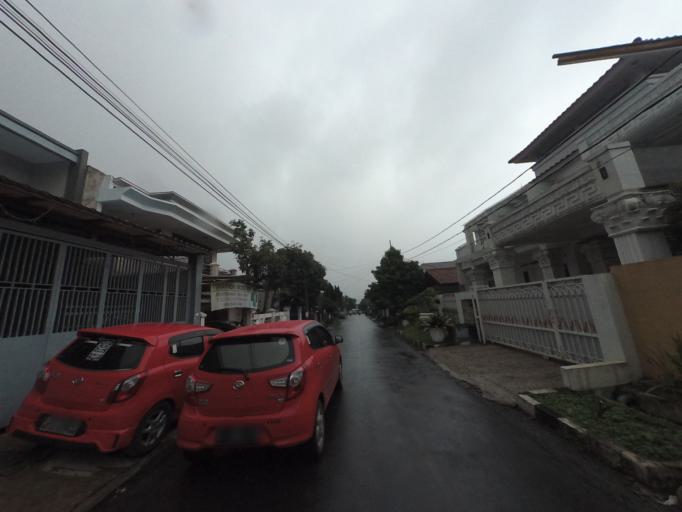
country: ID
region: West Java
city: Bogor
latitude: -6.5701
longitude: 106.7935
